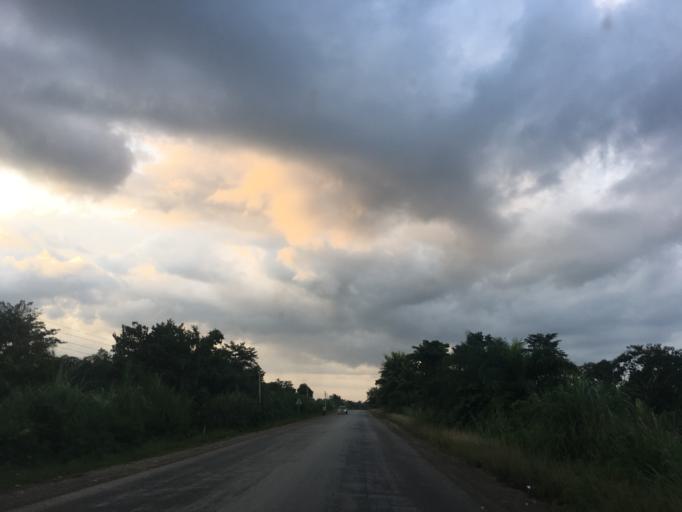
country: GH
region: Western
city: Bibiani
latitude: 6.7527
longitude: -2.5045
